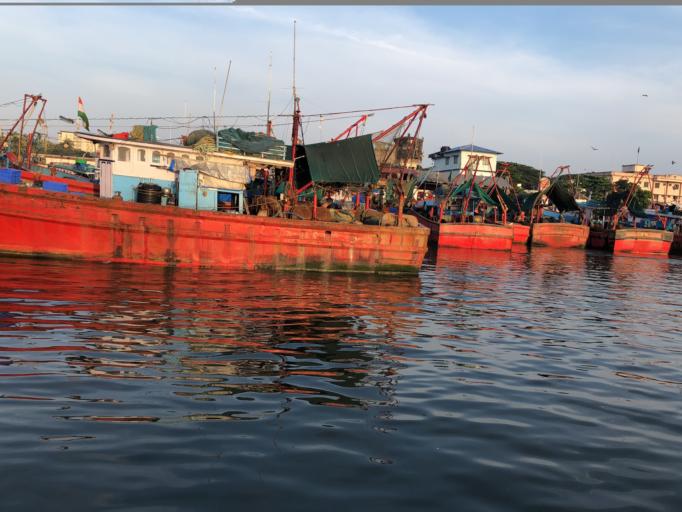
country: IN
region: Karnataka
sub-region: Dakshina Kannada
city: Ullal
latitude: 12.8556
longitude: 74.8325
